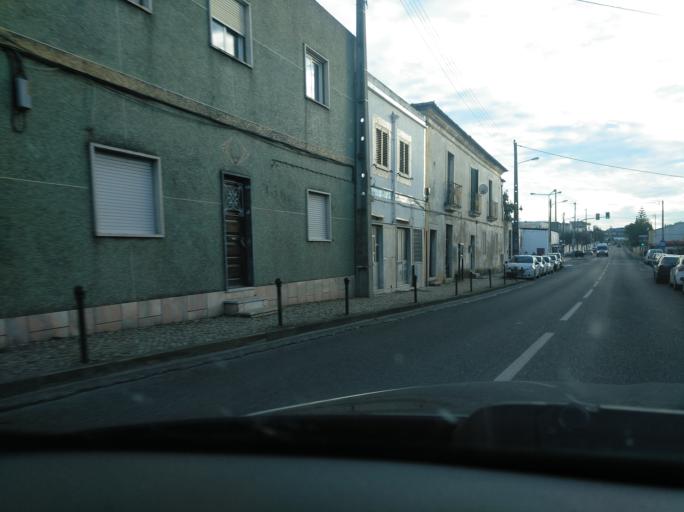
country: PT
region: Lisbon
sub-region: Loures
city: Apelacao
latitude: 38.8253
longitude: -9.1444
